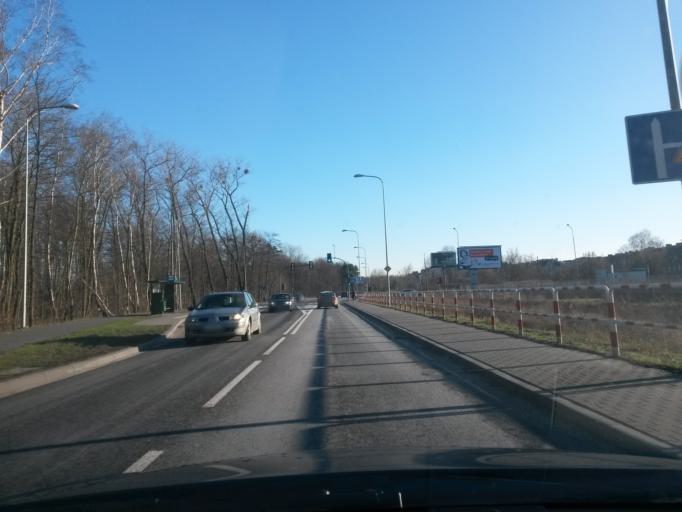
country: PL
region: Greater Poland Voivodeship
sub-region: Poznan
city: Poznan
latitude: 52.3924
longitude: 16.9979
